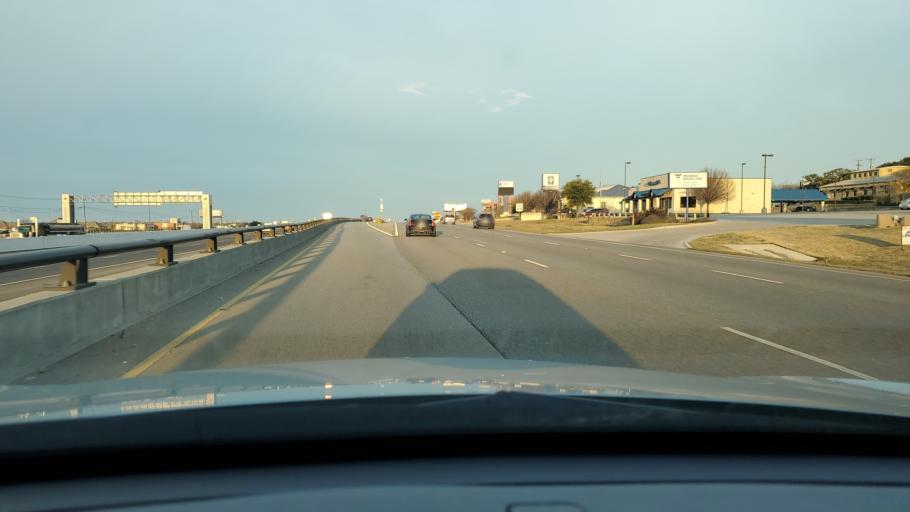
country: US
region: Texas
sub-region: Bell County
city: Harker Heights
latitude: 31.0739
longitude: -97.6798
